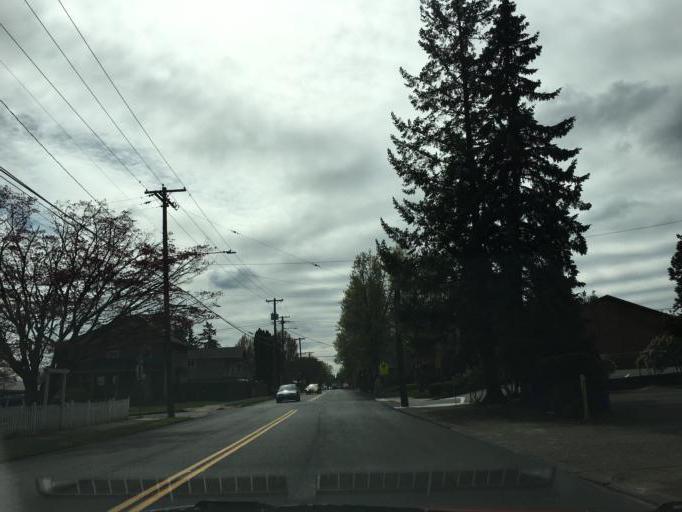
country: US
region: Oregon
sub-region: Clackamas County
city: Milwaukie
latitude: 45.4680
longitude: -122.6470
